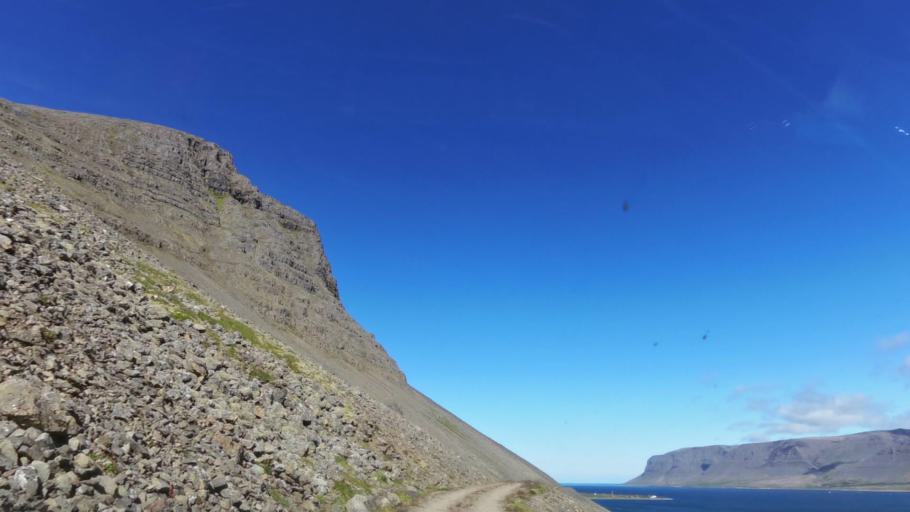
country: IS
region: West
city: Olafsvik
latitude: 65.6291
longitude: -23.9085
